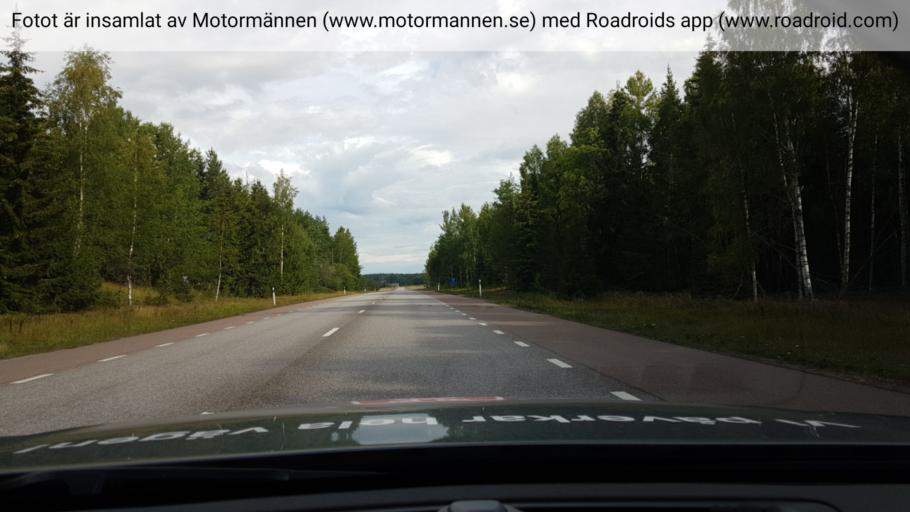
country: SE
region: Uppsala
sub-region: Heby Kommun
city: Morgongava
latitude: 59.8689
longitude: 16.9250
